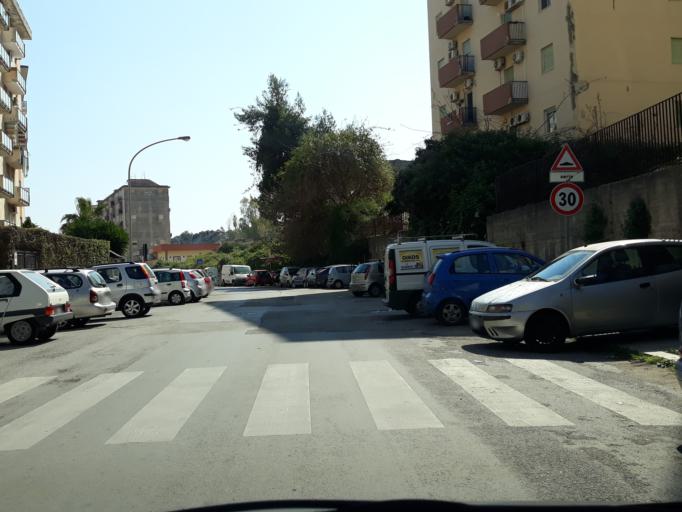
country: IT
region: Sicily
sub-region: Palermo
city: Piano dei Geli
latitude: 38.1248
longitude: 13.2921
